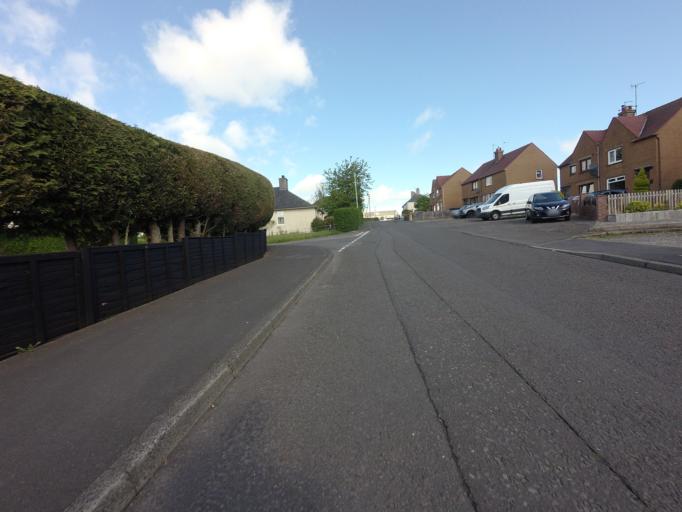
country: GB
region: Scotland
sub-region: Perth and Kinross
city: Auchterarder
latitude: 56.2934
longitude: -3.7089
